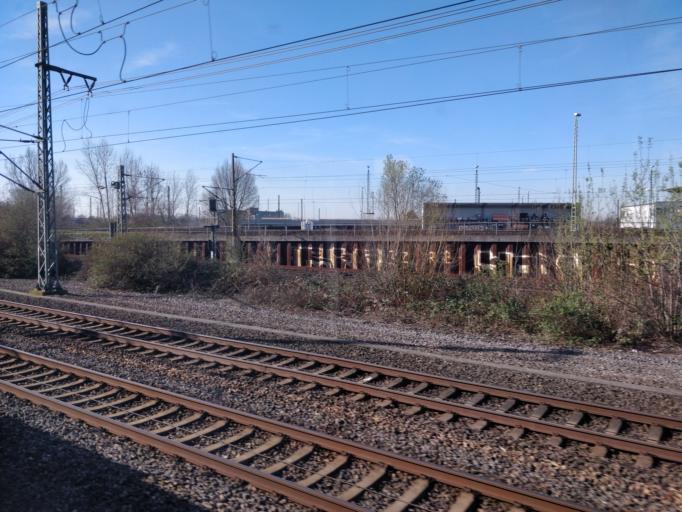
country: DE
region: North Rhine-Westphalia
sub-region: Regierungsbezirk Koln
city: Gremberghoven
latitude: 50.8986
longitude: 7.0555
